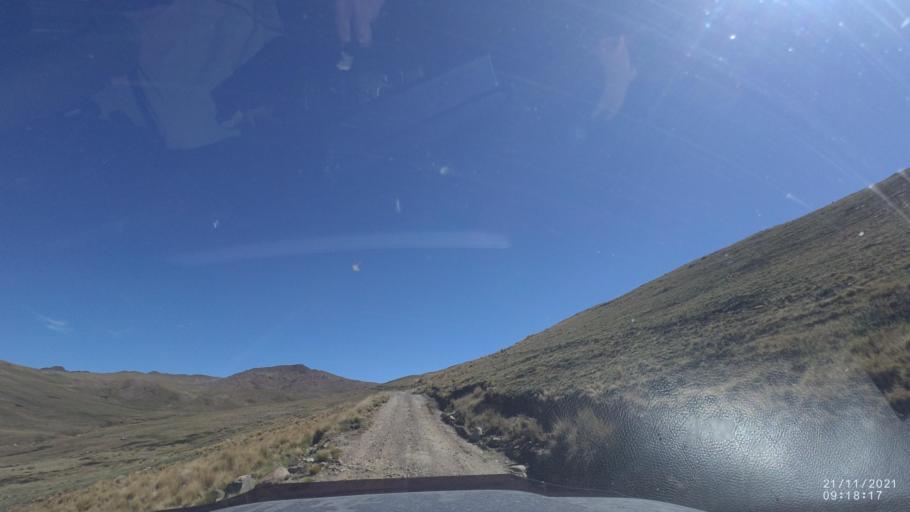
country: BO
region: Cochabamba
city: Cochabamba
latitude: -17.1198
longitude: -66.2568
